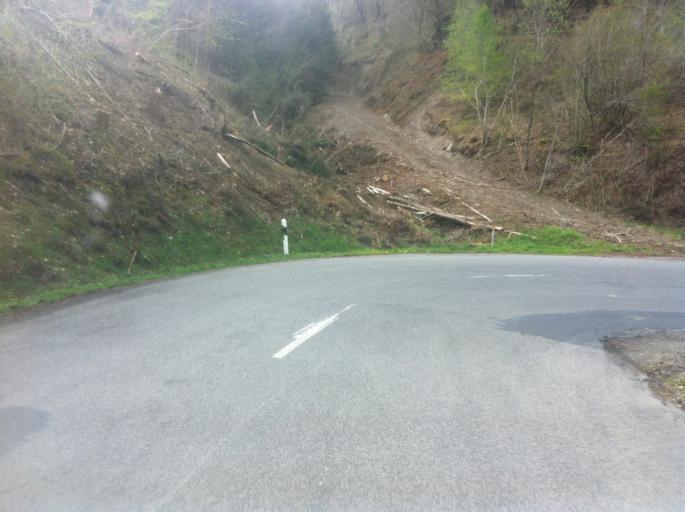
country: DE
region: Rheinland-Pfalz
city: Dasburg
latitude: 50.0514
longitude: 6.1217
